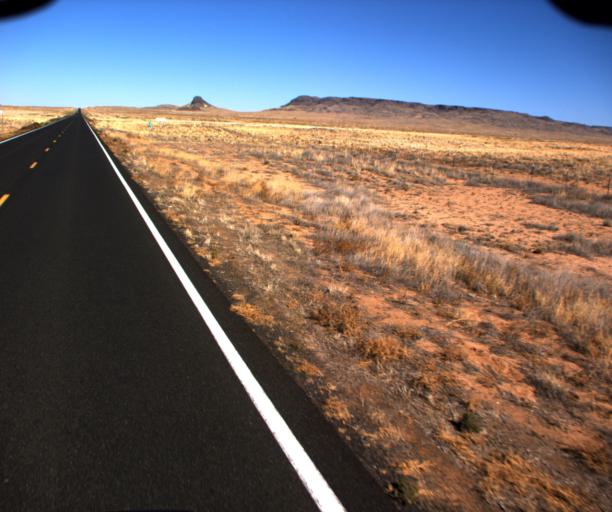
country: US
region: Arizona
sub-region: Navajo County
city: Dilkon
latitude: 35.3731
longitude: -110.4251
